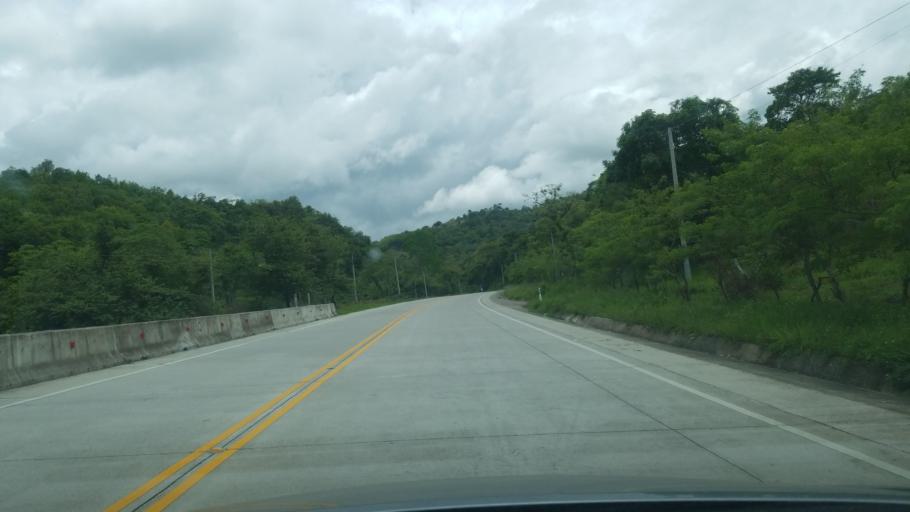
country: HN
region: Copan
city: Florida
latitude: 14.9997
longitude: -88.8397
